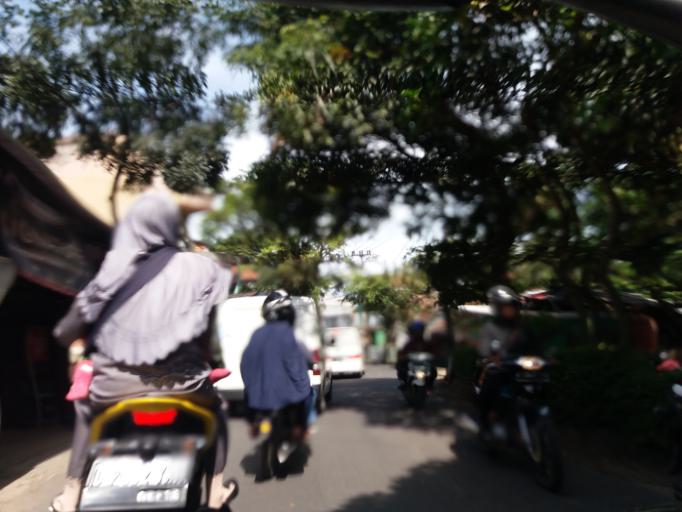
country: ID
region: West Java
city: Margahayukencana
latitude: -6.9515
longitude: 107.5773
